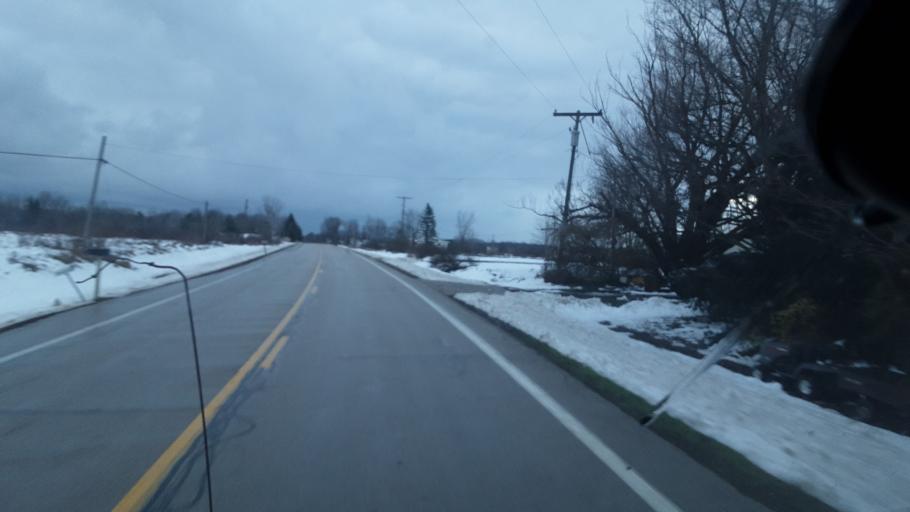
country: US
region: Ohio
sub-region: Ashtabula County
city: Jefferson
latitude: 41.6985
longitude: -80.7038
